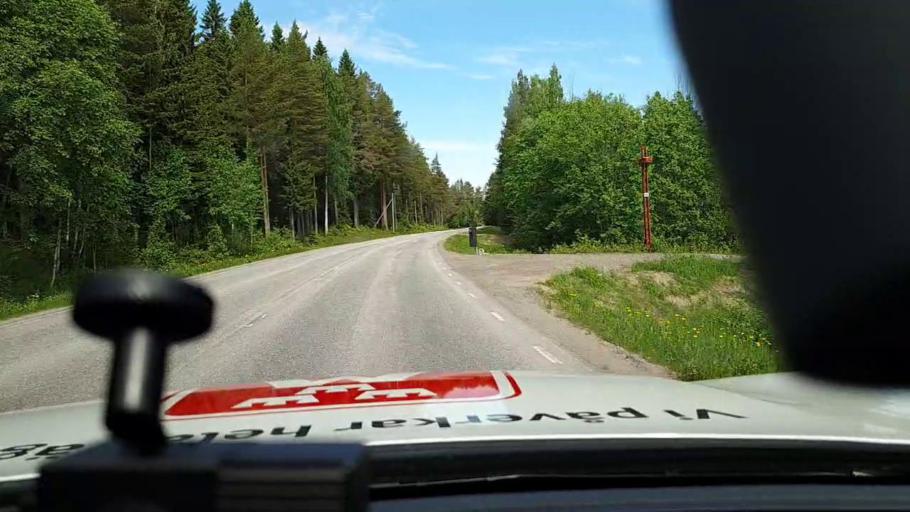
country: SE
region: Norrbotten
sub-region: Lulea Kommun
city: Gammelstad
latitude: 65.5903
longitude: 22.0016
